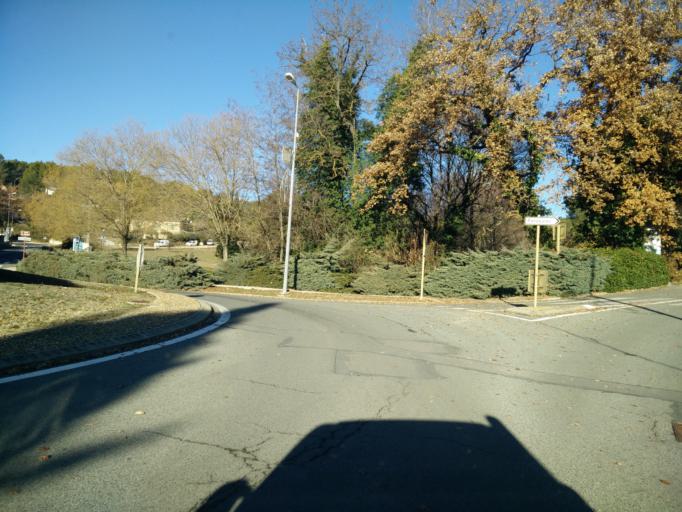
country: FR
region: Provence-Alpes-Cote d'Azur
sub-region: Departement du Var
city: Salernes
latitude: 43.5660
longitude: 6.2286
